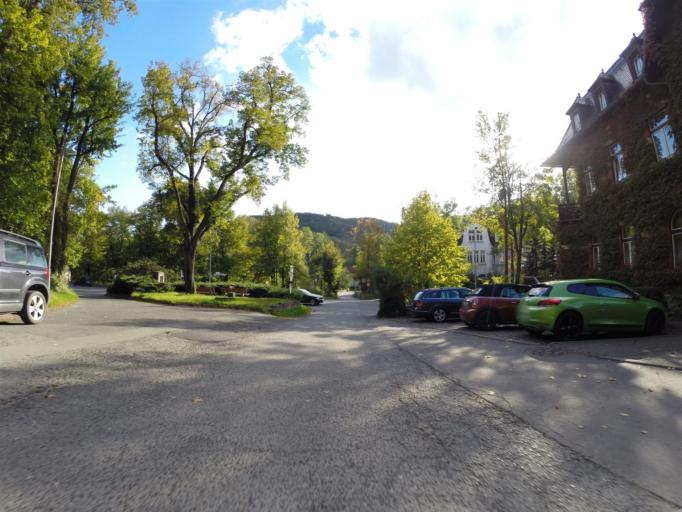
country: DE
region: Thuringia
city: Jena
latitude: 50.9375
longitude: 11.5584
